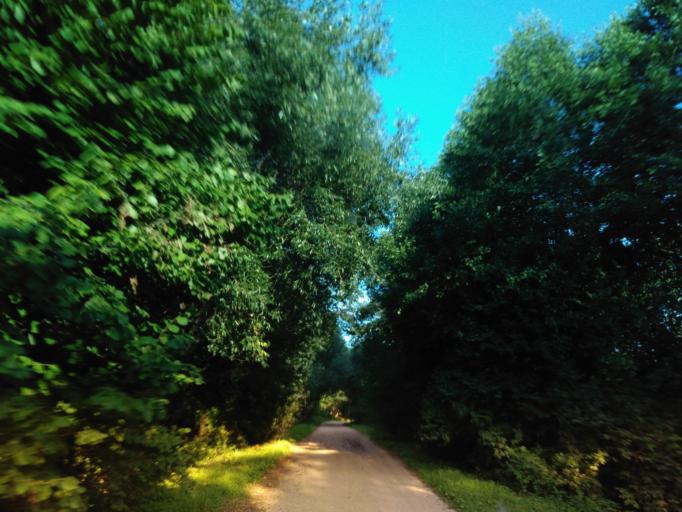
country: BY
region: Minsk
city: Uzda
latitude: 53.3461
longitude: 27.0904
